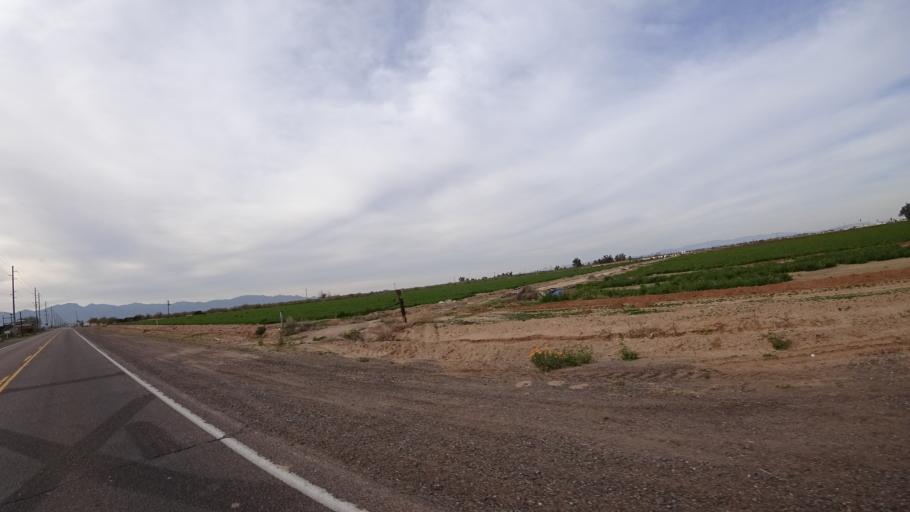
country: US
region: Arizona
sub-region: Maricopa County
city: El Mirage
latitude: 33.5658
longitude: -112.3650
